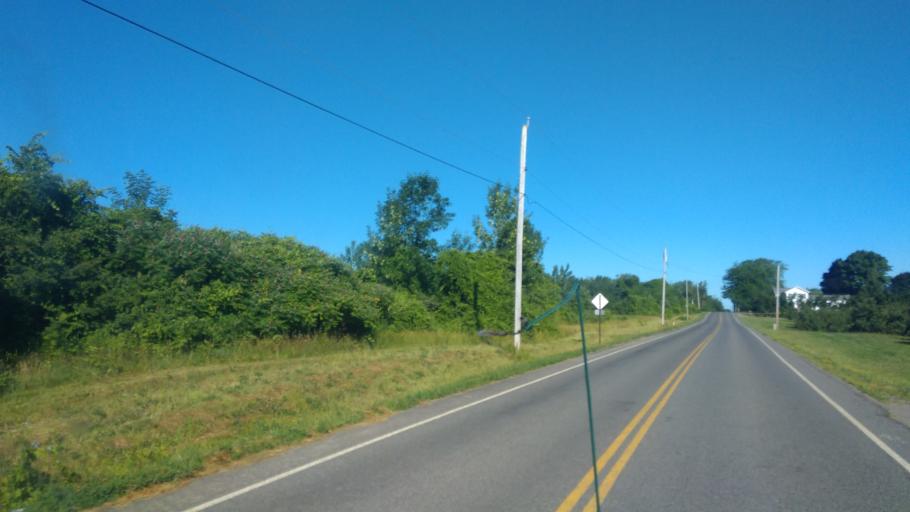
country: US
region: New York
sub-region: Wayne County
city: Sodus
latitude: 43.2776
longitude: -77.1198
